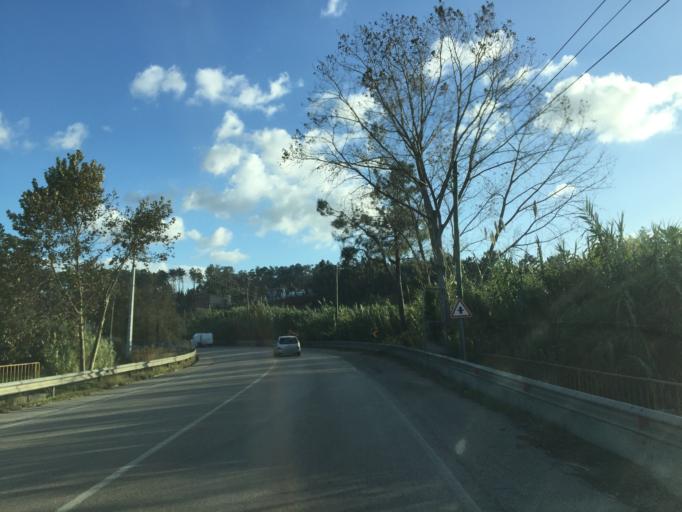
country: PT
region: Leiria
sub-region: Leiria
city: Souto da Carpalhosa
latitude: 39.8628
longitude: -8.8390
